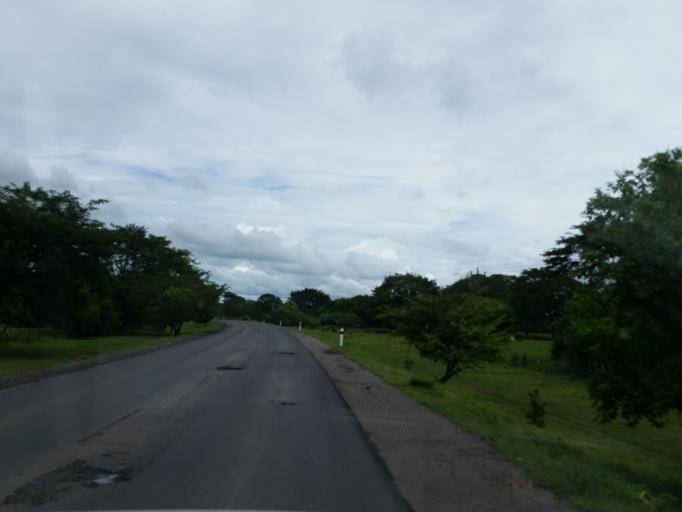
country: NI
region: Chinandega
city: Somotillo
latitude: 12.8416
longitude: -86.8819
